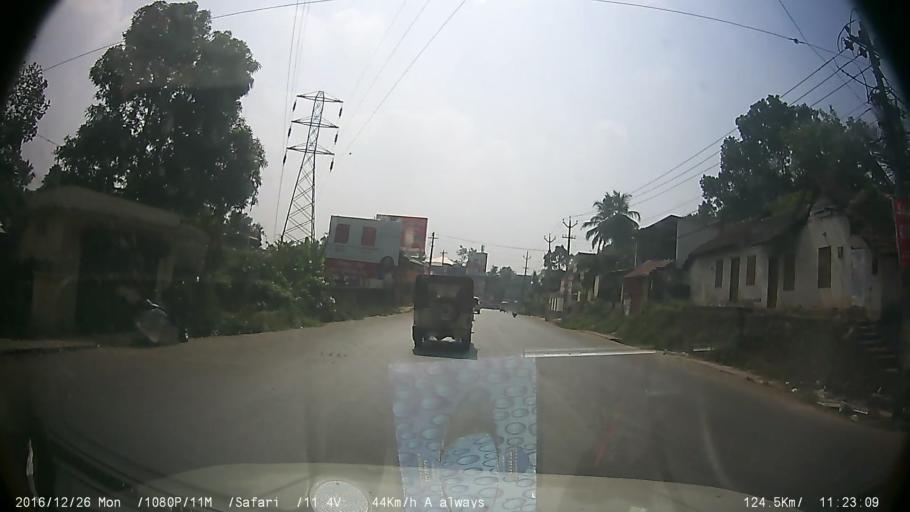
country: IN
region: Kerala
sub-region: Kottayam
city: Kottayam
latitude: 9.6066
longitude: 76.5318
